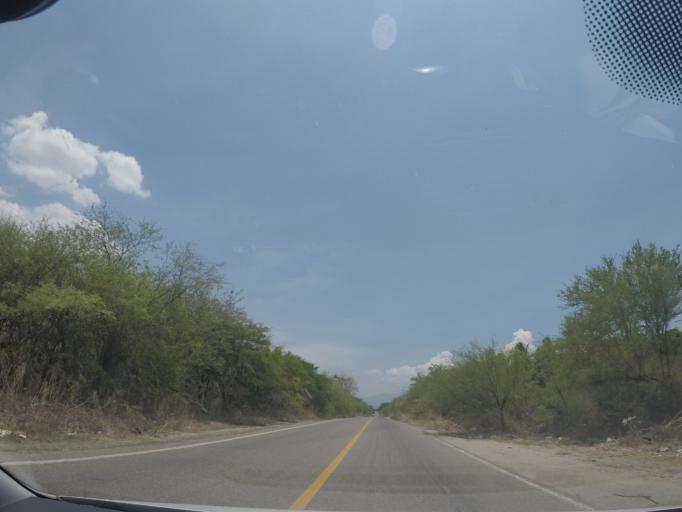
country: MX
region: Oaxaca
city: Santa Maria Jalapa del Marques
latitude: 16.4396
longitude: -95.4848
